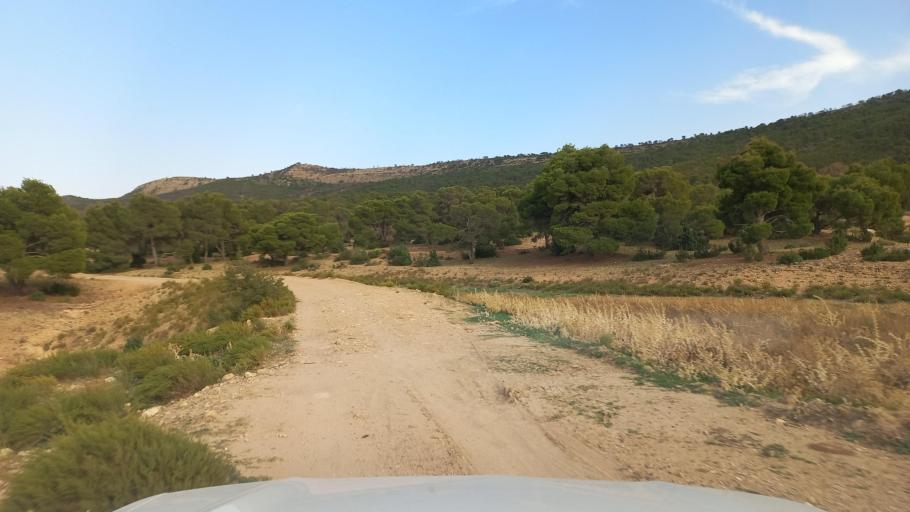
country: TN
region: Al Qasrayn
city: Kasserine
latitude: 35.3335
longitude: 8.8497
